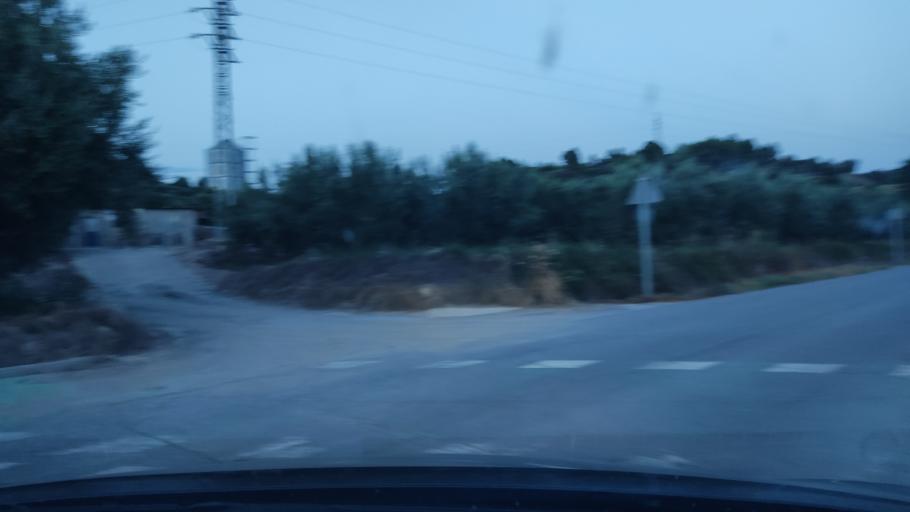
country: ES
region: Valencia
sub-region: Provincia de Castello
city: Jerica
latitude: 39.9082
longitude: -0.5604
